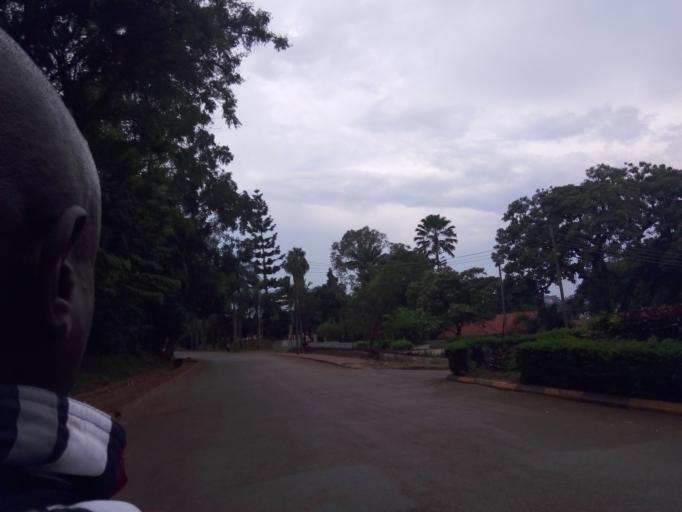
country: UG
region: Central Region
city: Kampala Central Division
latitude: 0.3264
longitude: 32.5822
